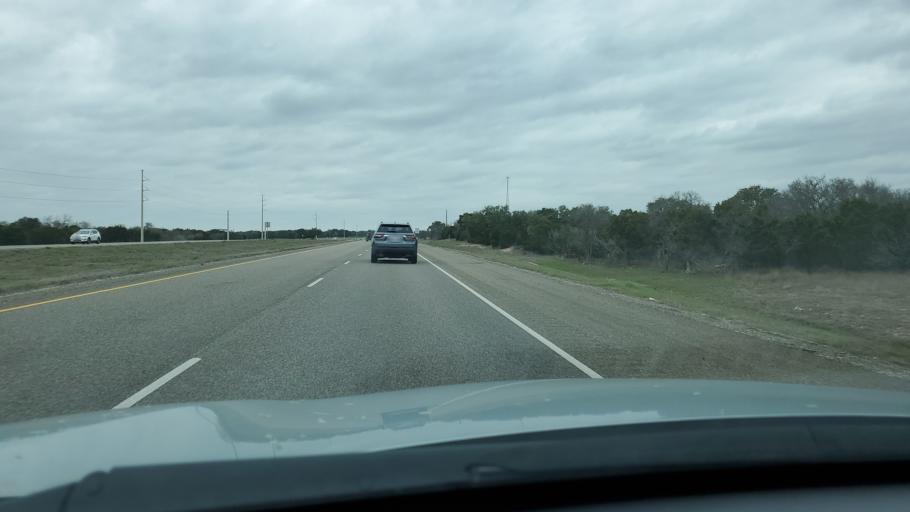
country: US
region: Texas
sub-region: Williamson County
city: Serenada
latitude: 30.7651
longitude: -97.7488
